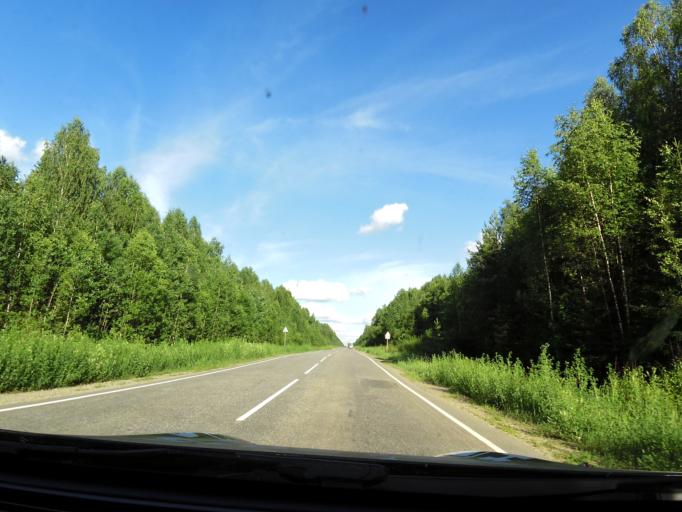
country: RU
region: Kirov
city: Chernaya Kholunitsa
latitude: 58.7722
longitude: 51.9470
